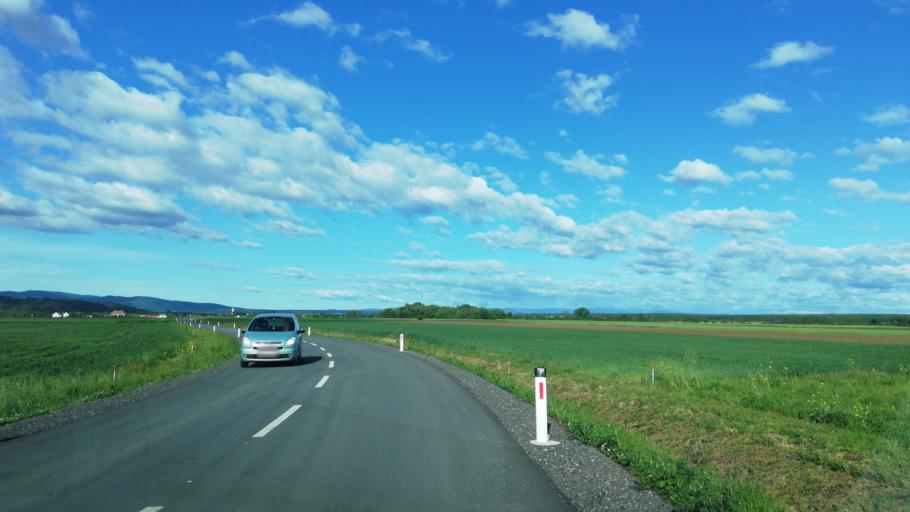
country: AT
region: Burgenland
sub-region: Politischer Bezirk Oberpullendorf
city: Lutzmannsburg
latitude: 47.4725
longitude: 16.6661
